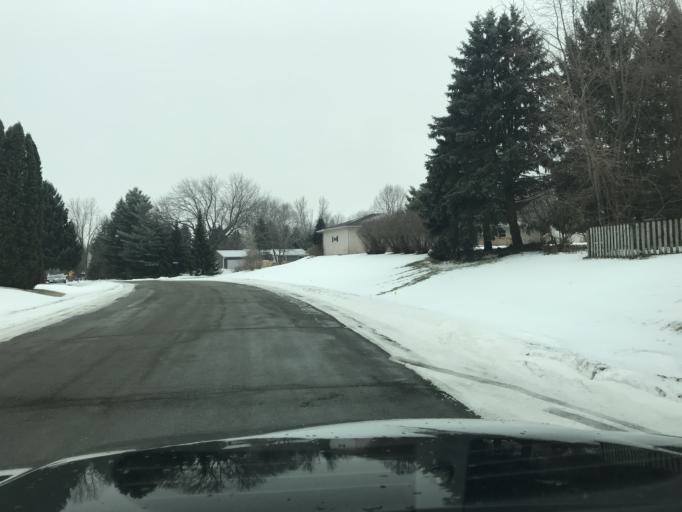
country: US
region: Wisconsin
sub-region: Dane County
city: Cottage Grove
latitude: 43.1022
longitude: -89.2155
